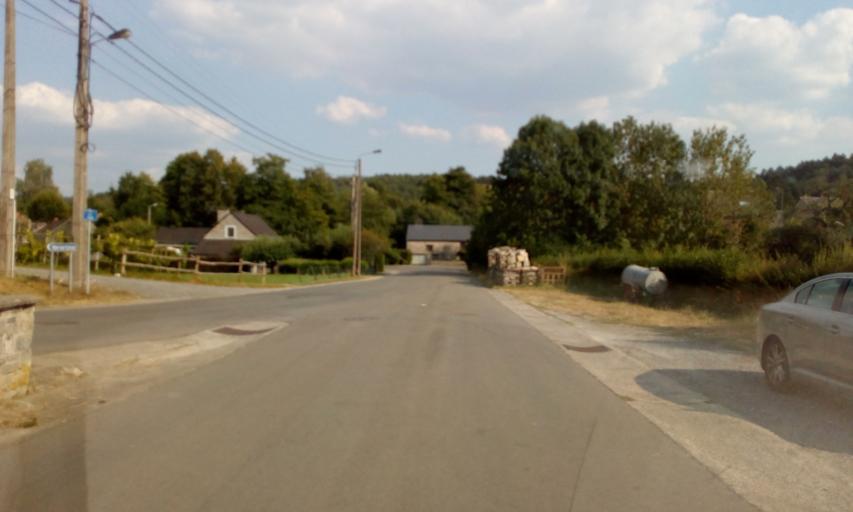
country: BE
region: Wallonia
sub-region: Province du Luxembourg
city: Tellin
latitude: 50.1071
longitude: 5.1925
